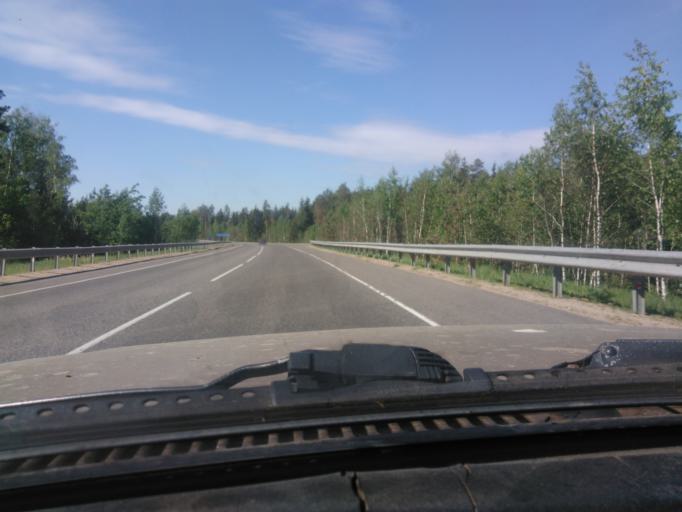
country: BY
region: Mogilev
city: Myazhysyatki
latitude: 53.8069
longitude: 30.2111
